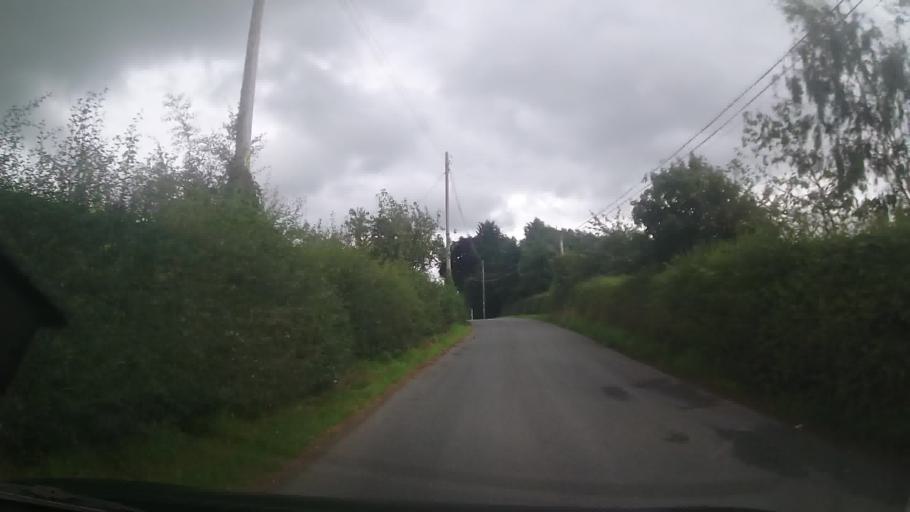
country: GB
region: England
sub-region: Shropshire
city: Whitchurch
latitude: 52.9476
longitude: -2.7317
